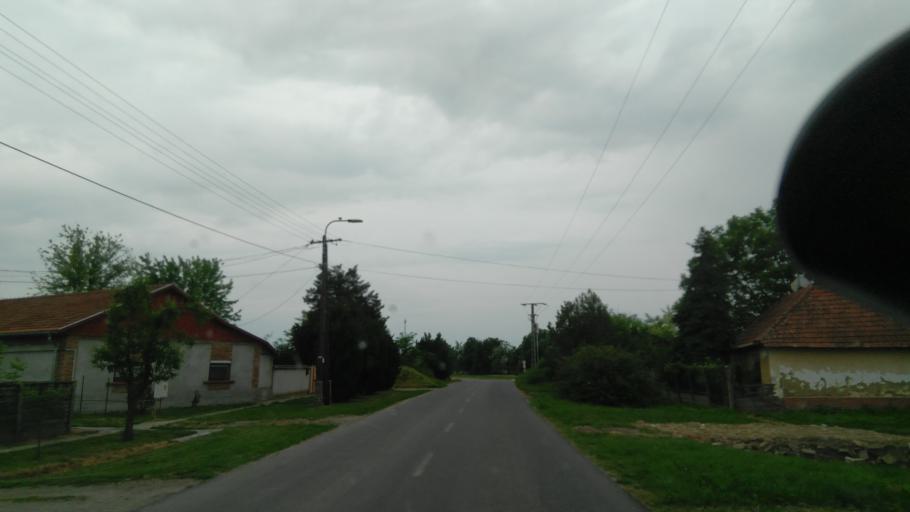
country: HU
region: Bekes
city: Doboz
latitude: 46.7263
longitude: 21.2409
